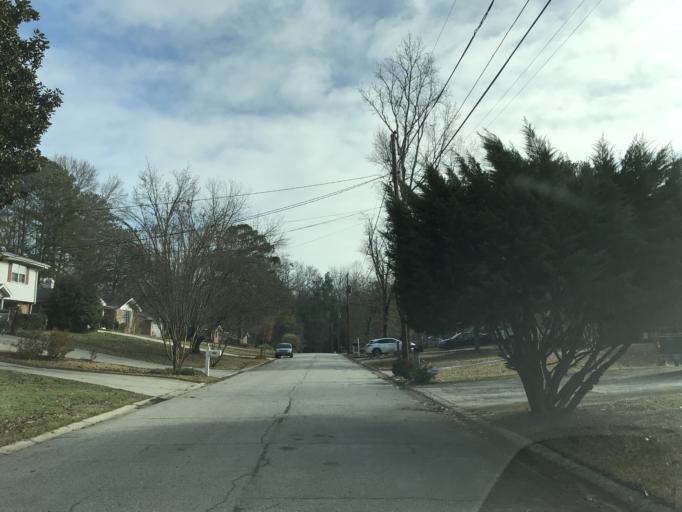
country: US
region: Georgia
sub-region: Clayton County
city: Morrow
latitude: 33.5627
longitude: -84.3651
